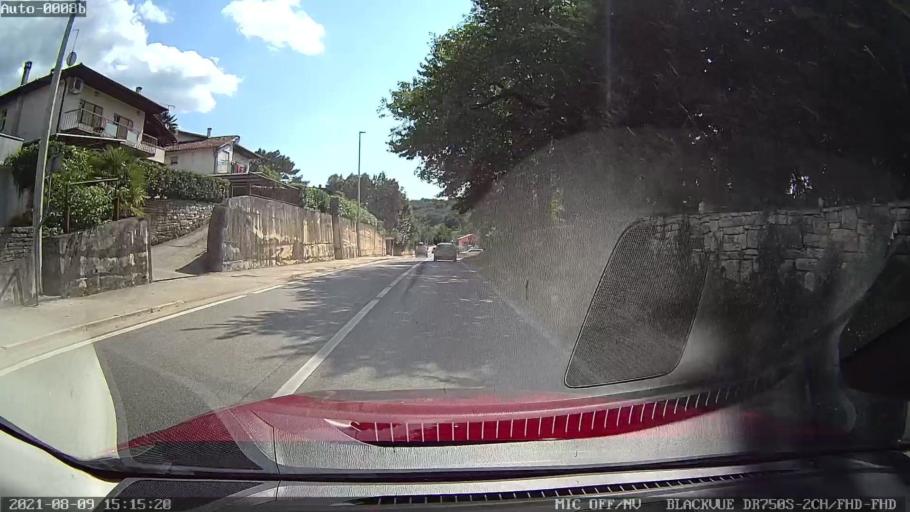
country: HR
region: Istarska
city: Pazin
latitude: 45.2365
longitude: 13.9242
